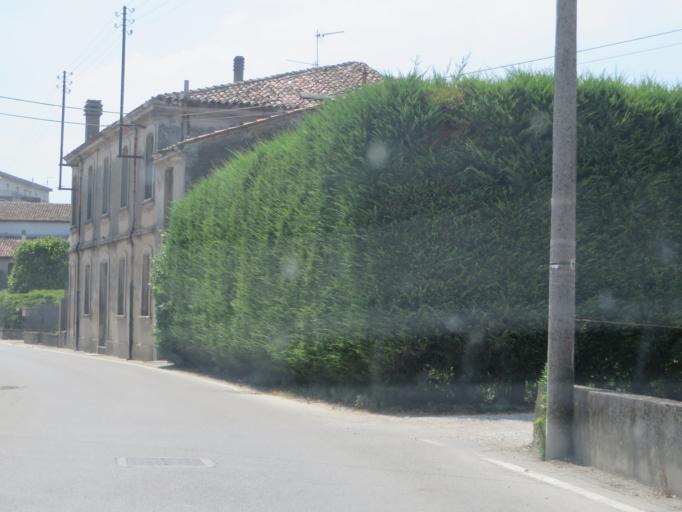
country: IT
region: Veneto
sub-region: Provincia di Verona
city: San Pietro di Morubio
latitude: 45.2450
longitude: 11.2294
